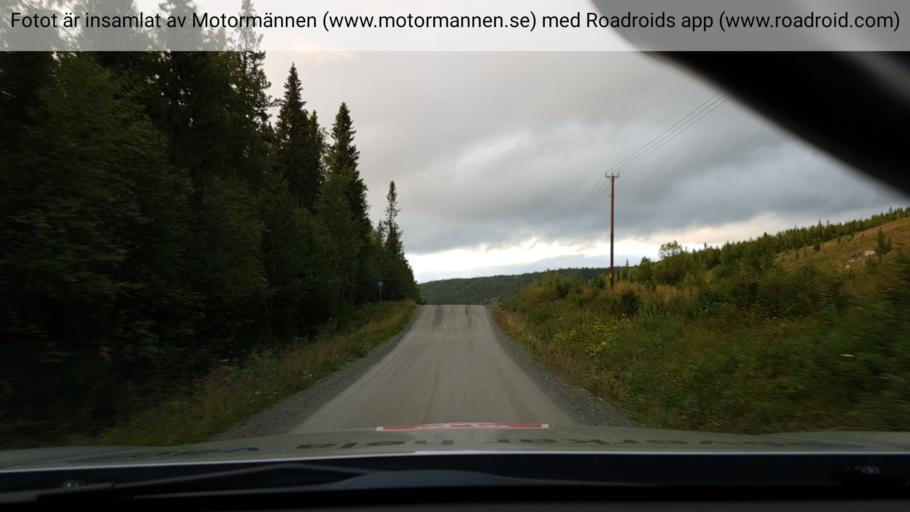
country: SE
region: Vaesterbotten
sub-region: Vilhelmina Kommun
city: Sjoberg
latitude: 65.5922
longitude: 15.2865
